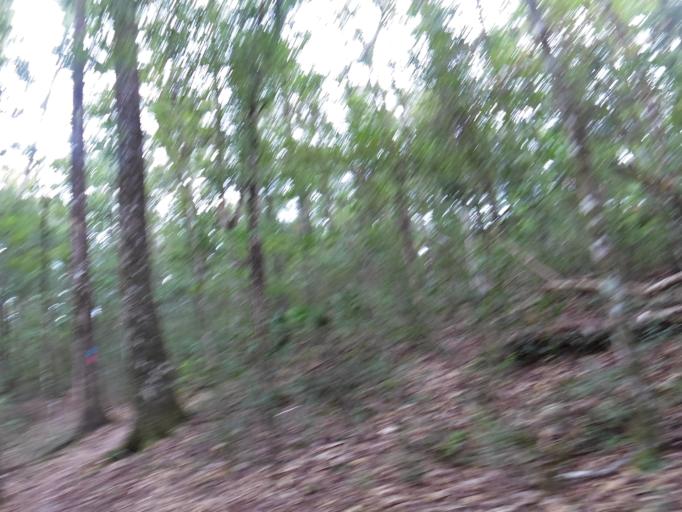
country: US
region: Florida
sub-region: Clay County
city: Middleburg
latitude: 30.1427
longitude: -81.9528
